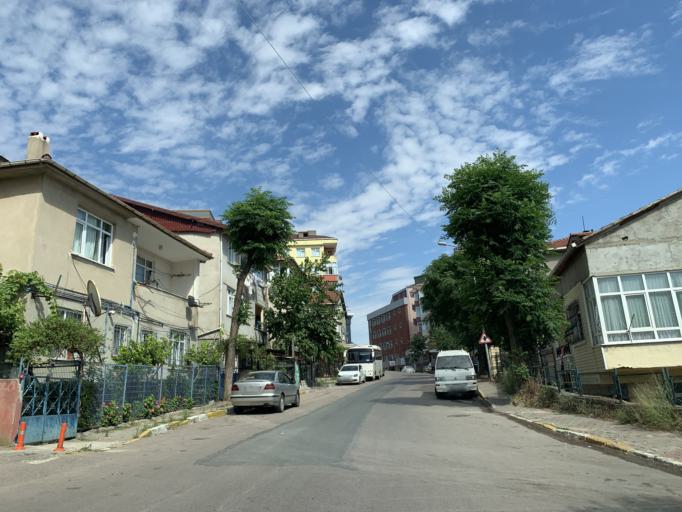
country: TR
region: Istanbul
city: Pendik
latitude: 40.8954
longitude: 29.2458
